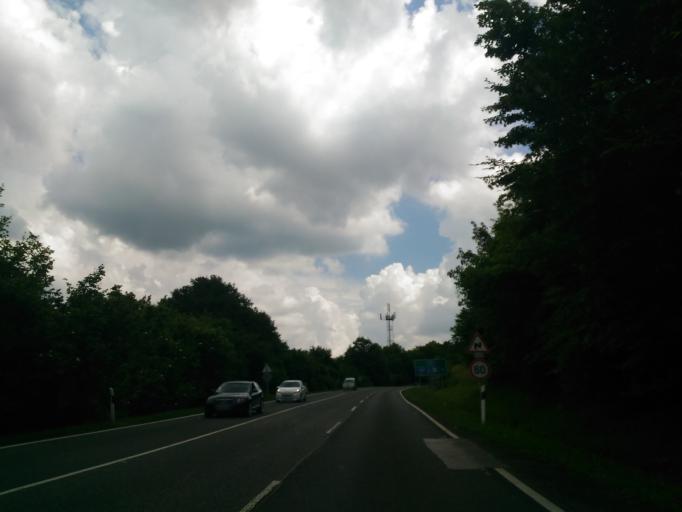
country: HU
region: Baranya
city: Komlo
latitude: 46.1572
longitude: 18.2398
